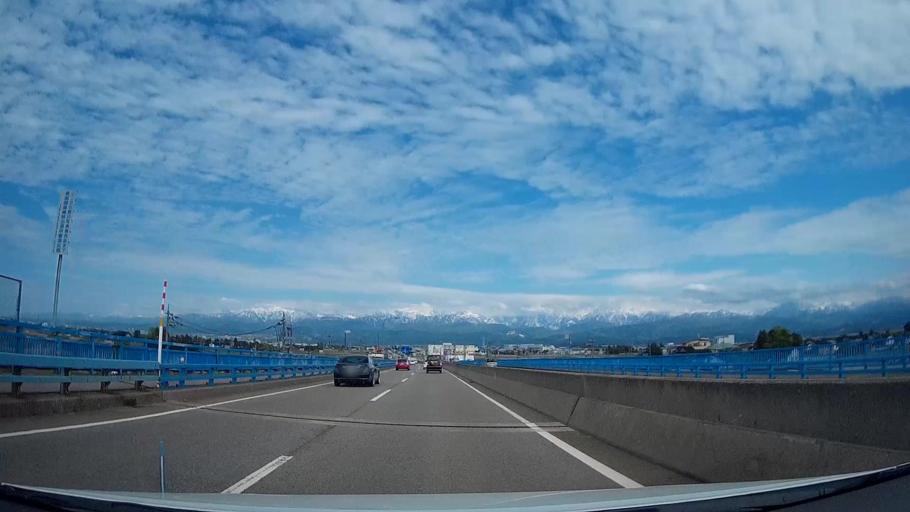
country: JP
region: Toyama
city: Toyama-shi
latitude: 36.7183
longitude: 137.2770
